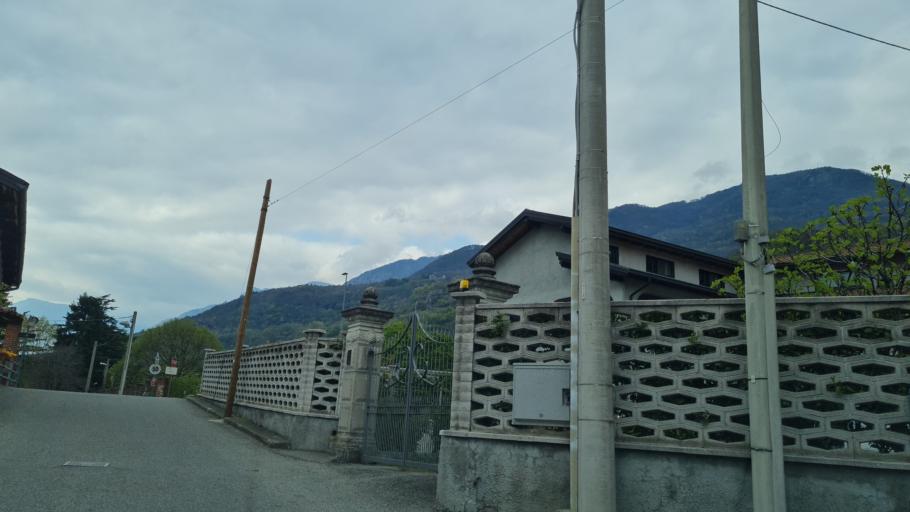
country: IT
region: Piedmont
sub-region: Provincia di Torino
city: Borgofranco d'Ivrea
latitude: 45.5257
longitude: 7.8521
